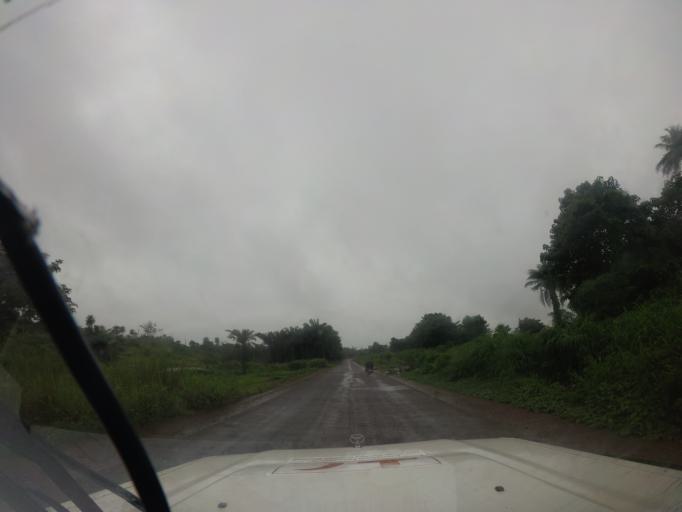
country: SL
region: Northern Province
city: Binkolo
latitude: 8.9262
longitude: -12.0147
